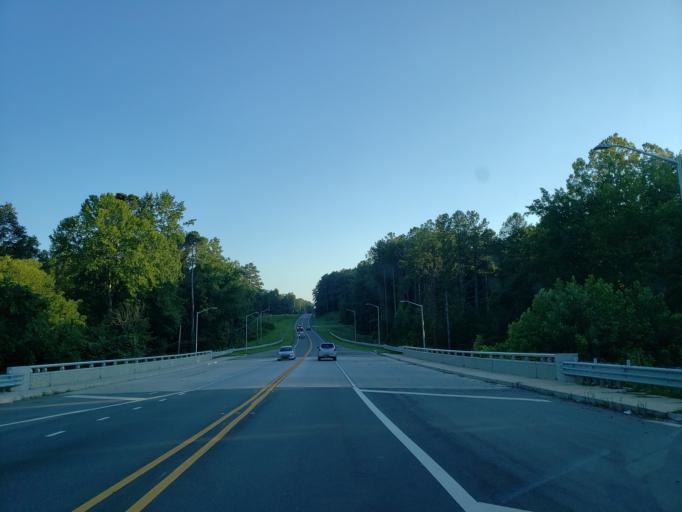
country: US
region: Georgia
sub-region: Paulding County
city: Dallas
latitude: 33.9966
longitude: -84.7645
